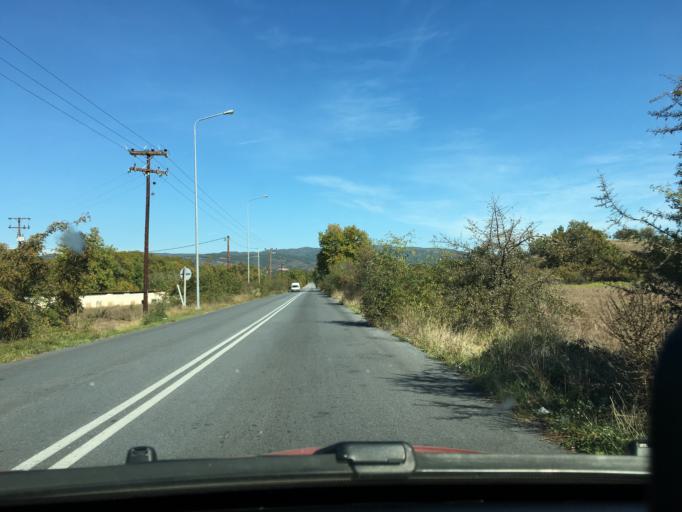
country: GR
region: Central Macedonia
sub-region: Nomos Chalkidikis
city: Megali Panagia
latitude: 40.3688
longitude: 23.6922
